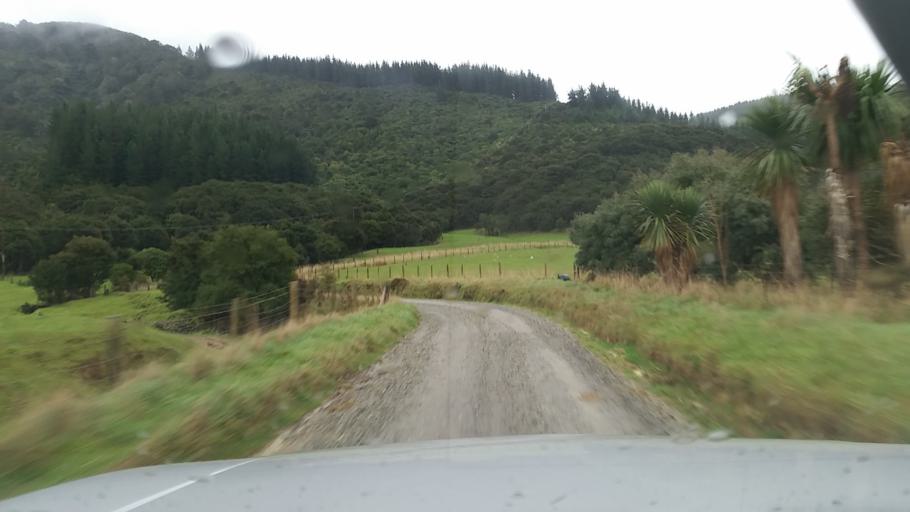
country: NZ
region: Marlborough
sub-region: Marlborough District
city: Picton
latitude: -41.1484
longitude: 174.0513
